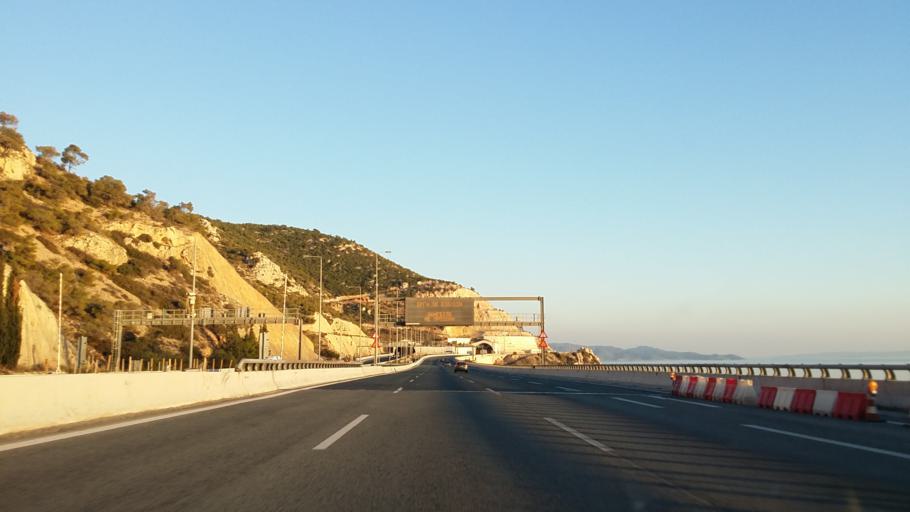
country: GR
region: Attica
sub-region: Nomarchia Dytikis Attikis
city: Megara
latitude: 37.9777
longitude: 23.2828
